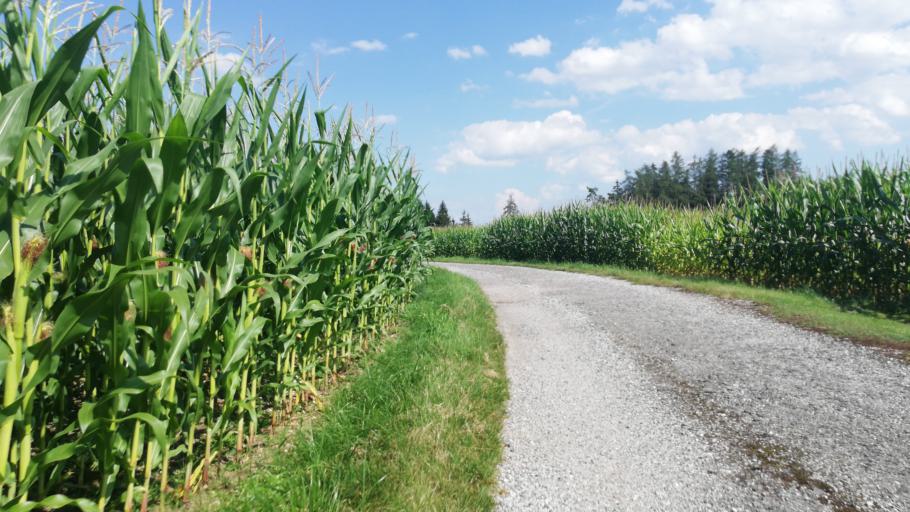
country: AT
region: Upper Austria
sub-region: Wels-Land
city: Offenhausen
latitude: 48.1608
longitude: 13.8602
